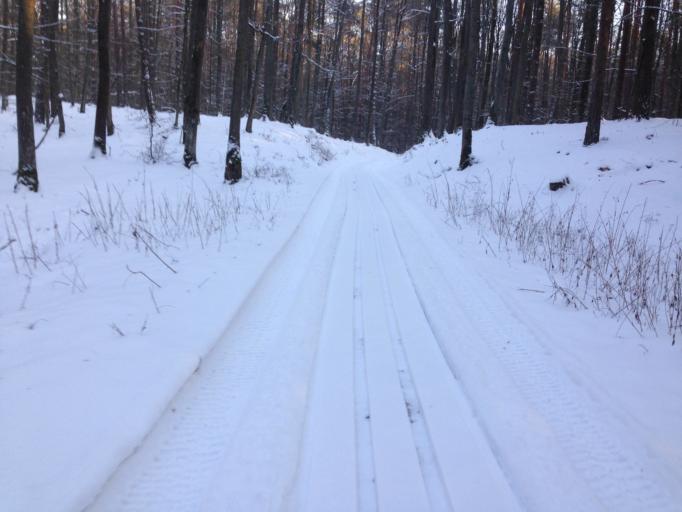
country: PL
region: Kujawsko-Pomorskie
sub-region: Powiat brodnicki
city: Gorzno
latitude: 53.1946
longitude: 19.6713
